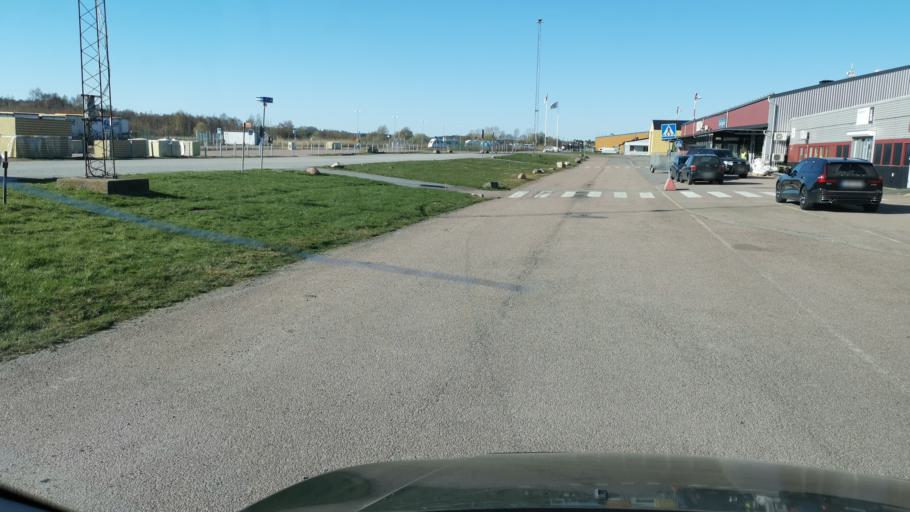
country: SE
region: Vaestra Goetaland
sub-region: Goteborg
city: Majorna
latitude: 57.7771
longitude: 11.8642
